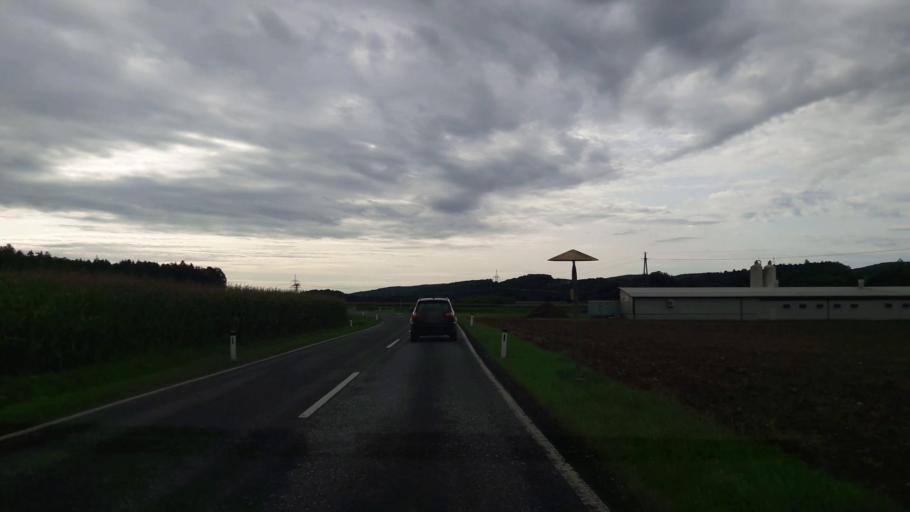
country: AT
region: Styria
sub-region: Politischer Bezirk Hartberg-Fuerstenfeld
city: Ebersdorf
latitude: 47.2119
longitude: 15.9330
